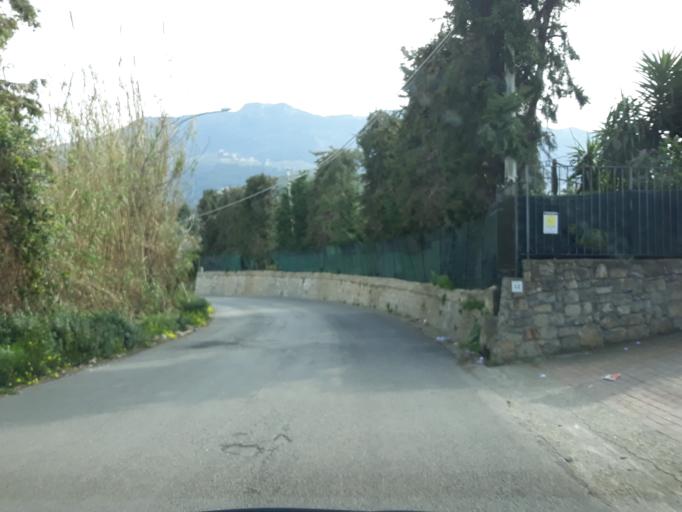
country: IT
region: Sicily
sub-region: Palermo
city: Monreale
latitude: 38.0710
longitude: 13.3041
